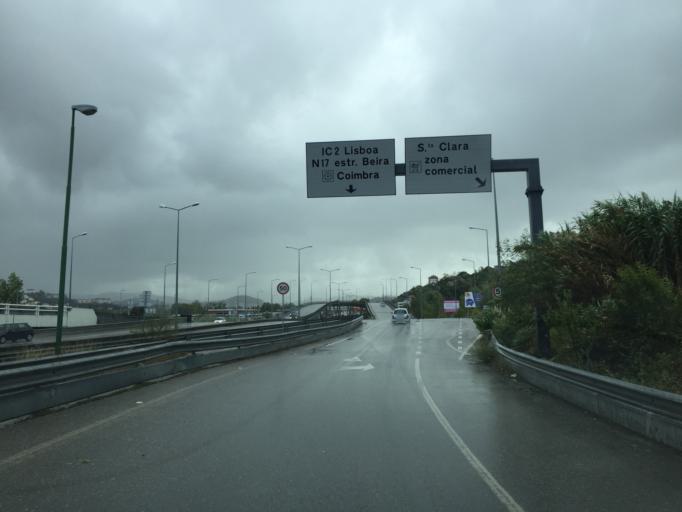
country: PT
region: Coimbra
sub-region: Coimbra
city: Coimbra
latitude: 40.2142
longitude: -8.4420
